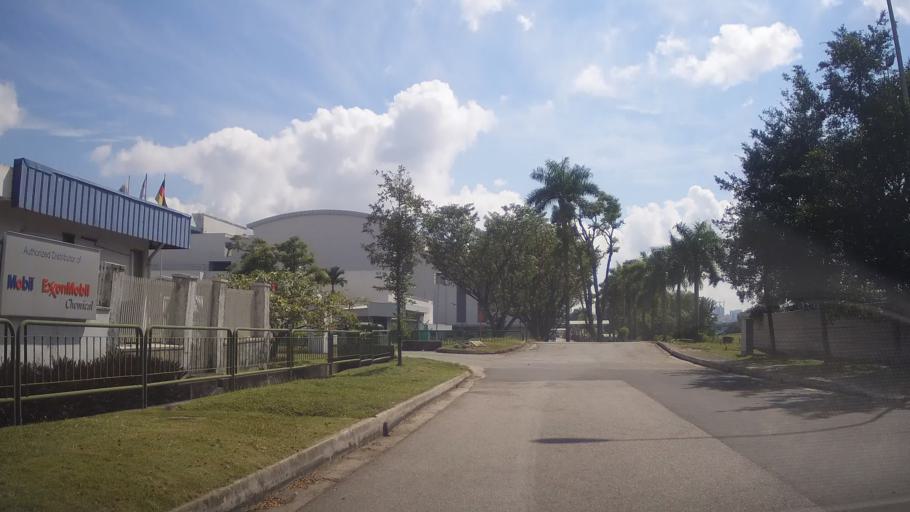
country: SG
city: Singapore
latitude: 1.3205
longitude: 103.7145
